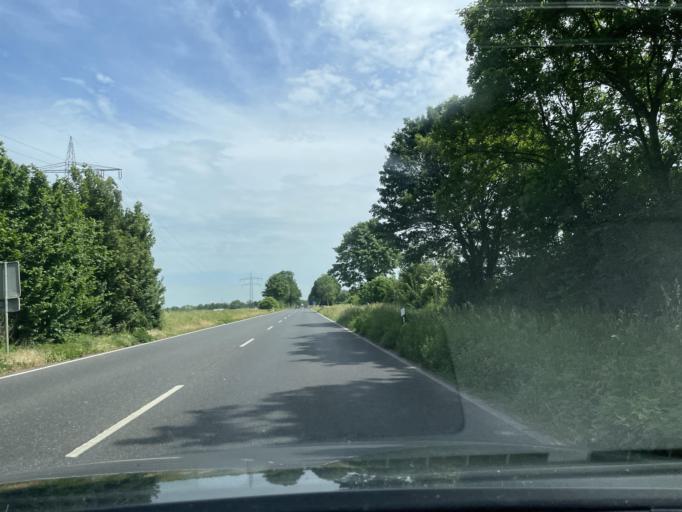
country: DE
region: North Rhine-Westphalia
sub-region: Regierungsbezirk Dusseldorf
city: Monchengladbach
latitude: 51.1187
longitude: 6.4169
